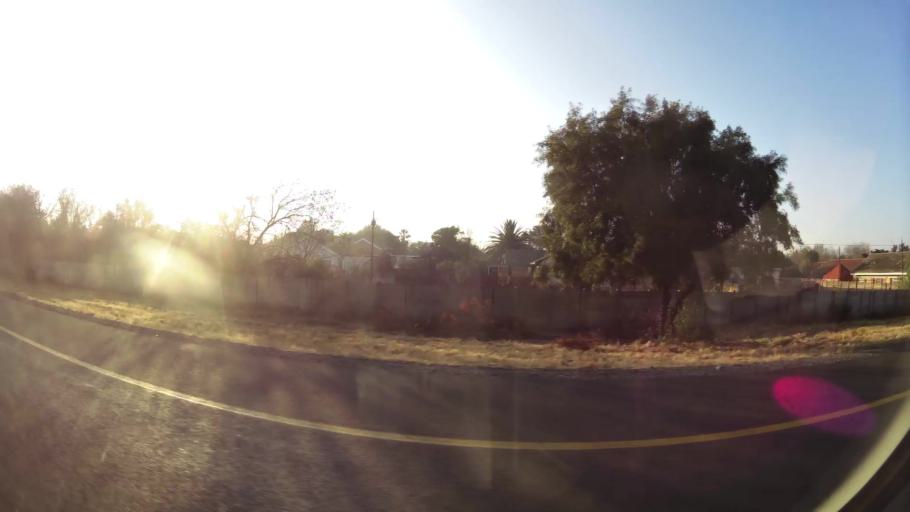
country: ZA
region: Orange Free State
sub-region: Mangaung Metropolitan Municipality
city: Bloemfontein
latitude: -29.1174
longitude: 26.1630
